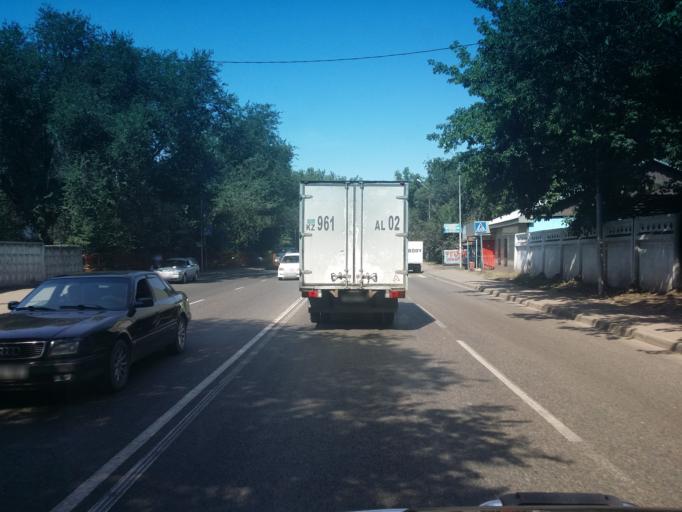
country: KZ
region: Almaty Oblysy
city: Pervomayskiy
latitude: 43.3482
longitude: 76.9660
